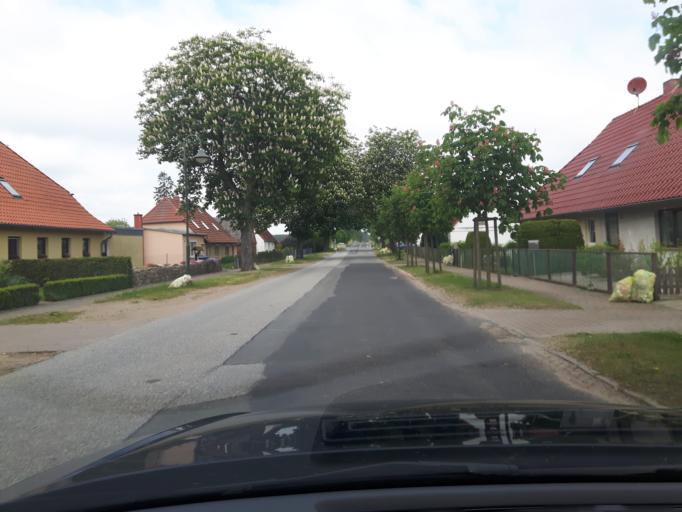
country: DE
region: Mecklenburg-Vorpommern
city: Grabowhofe
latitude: 53.5844
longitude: 12.5061
